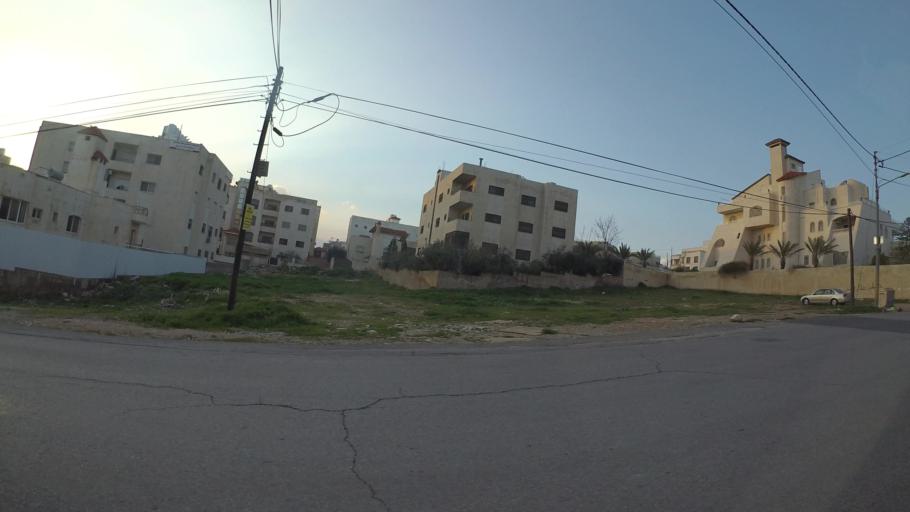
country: JO
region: Amman
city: Amman
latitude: 31.9921
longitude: 35.9505
